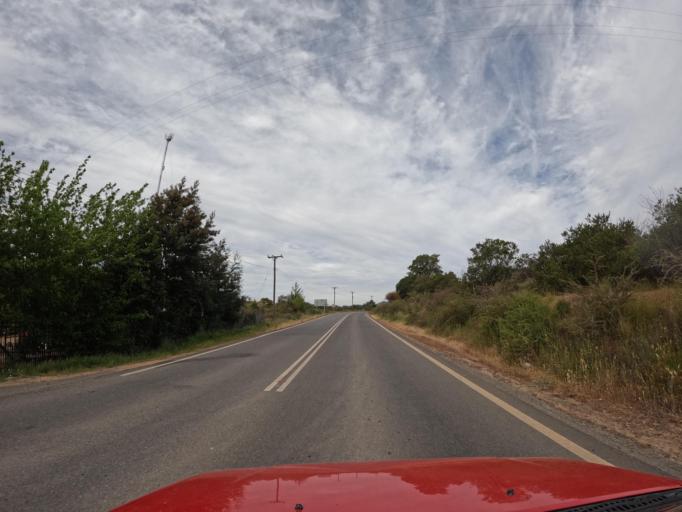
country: CL
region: Maule
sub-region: Provincia de Talca
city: Talca
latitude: -35.3228
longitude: -71.9349
